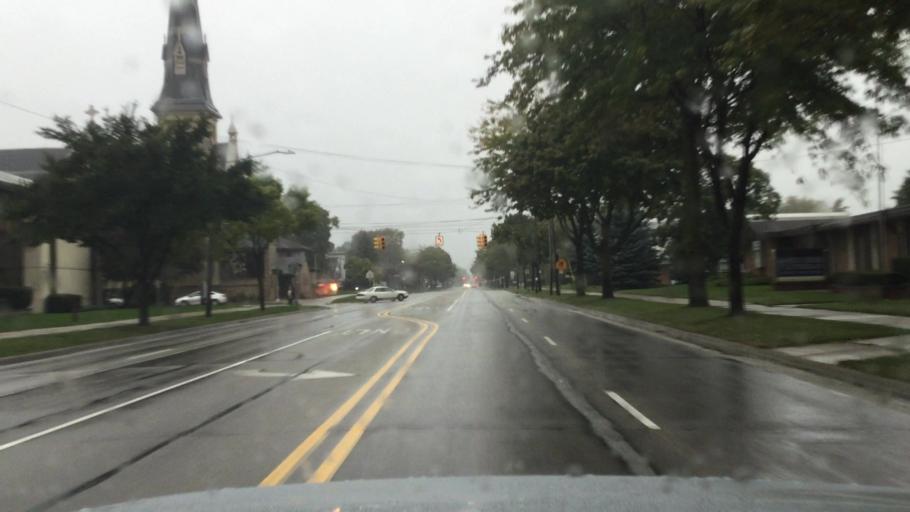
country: US
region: Michigan
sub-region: Saginaw County
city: Saginaw
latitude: 43.4183
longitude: -83.9653
